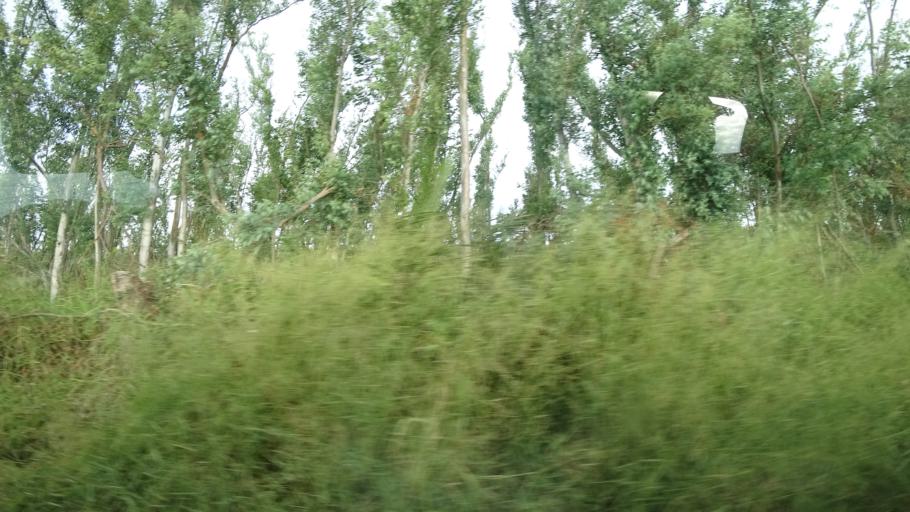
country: MZ
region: Sofala
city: Beira
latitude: -19.7692
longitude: 34.8904
